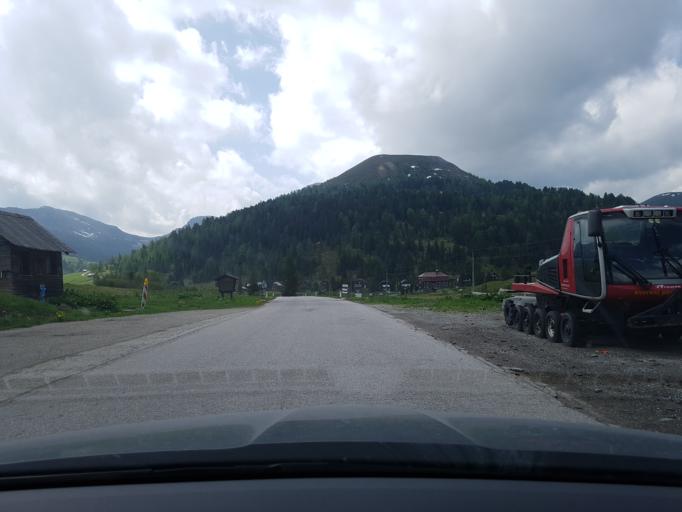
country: AT
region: Salzburg
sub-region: Politischer Bezirk Tamsweg
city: Thomatal
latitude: 46.9823
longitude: 13.7760
